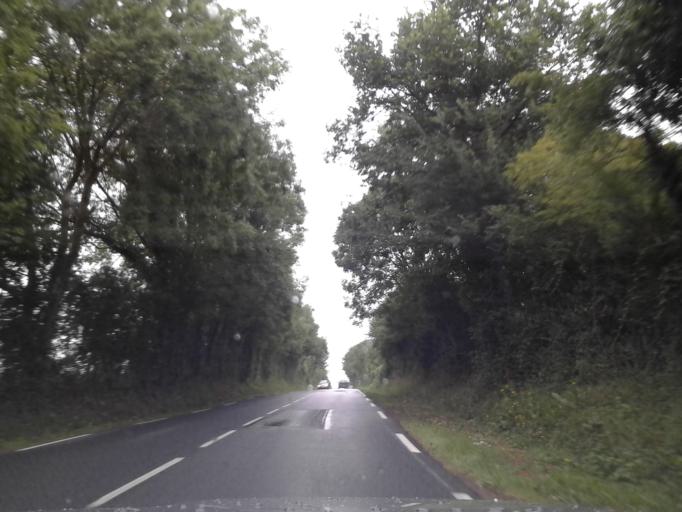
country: FR
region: Lower Normandy
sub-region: Departement de la Manche
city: Carentan
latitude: 49.3307
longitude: -1.2668
